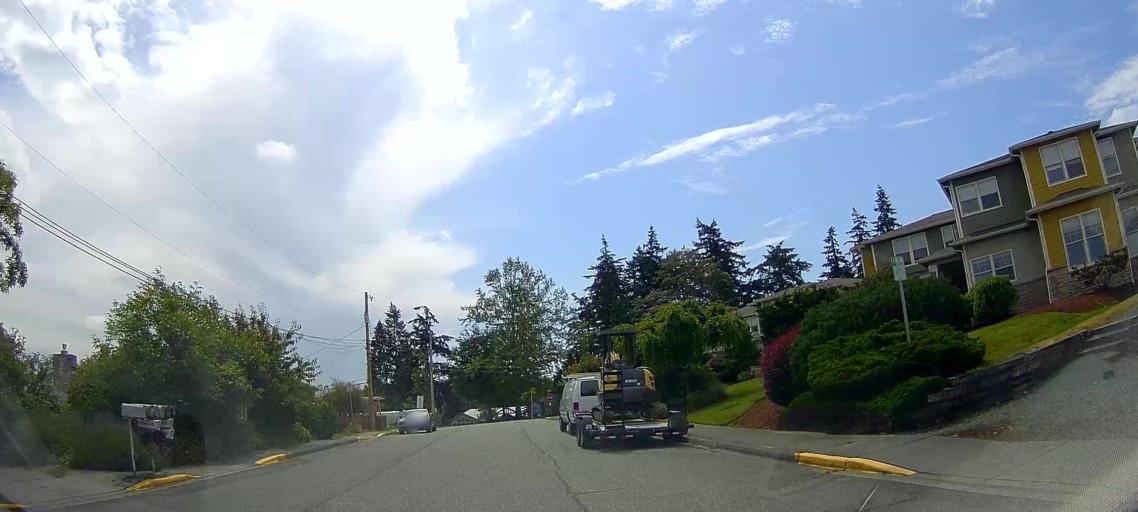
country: US
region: Washington
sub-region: Skagit County
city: Anacortes
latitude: 48.5053
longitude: -122.6236
